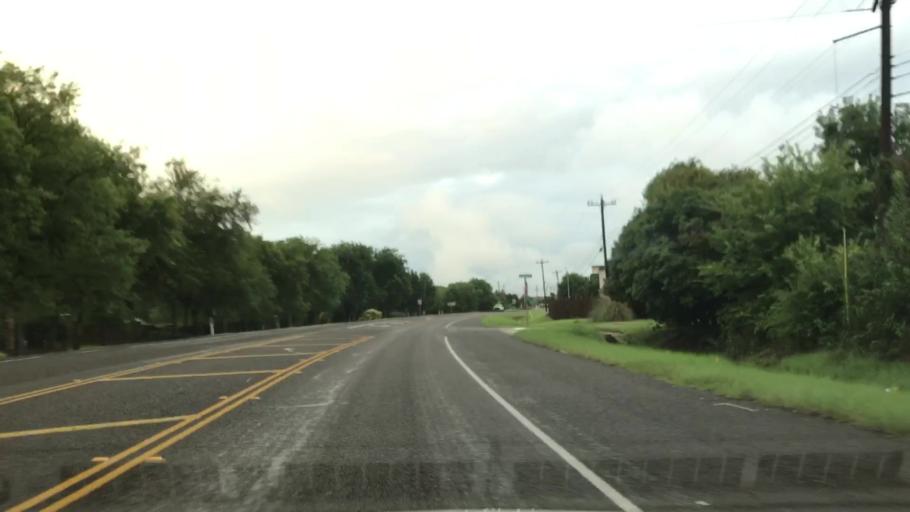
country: US
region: Texas
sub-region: Rockwall County
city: Rockwall
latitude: 32.9697
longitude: -96.4652
